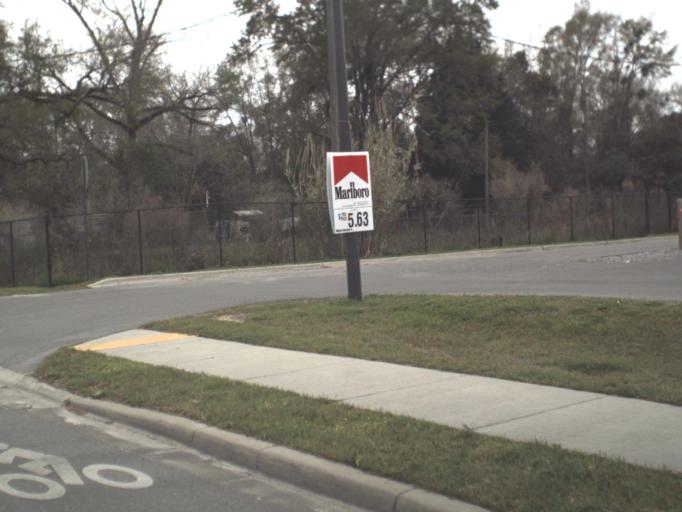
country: US
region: Florida
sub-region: Gulf County
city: Wewahitchka
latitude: 30.1054
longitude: -85.2006
